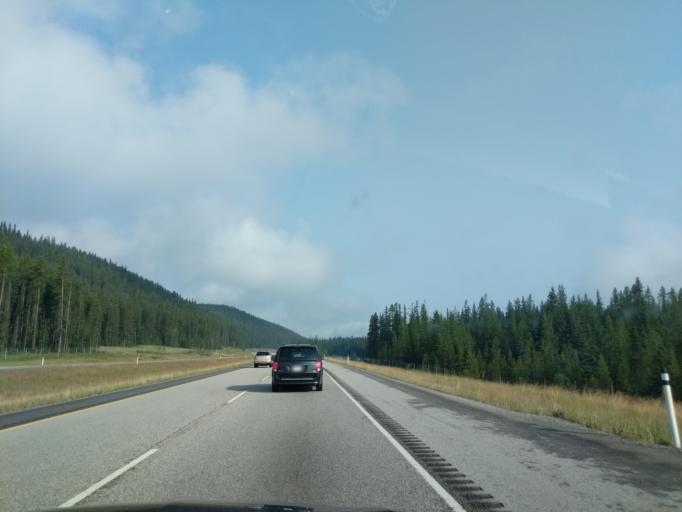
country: CA
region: Alberta
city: Lake Louise
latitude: 51.3226
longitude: -116.0414
